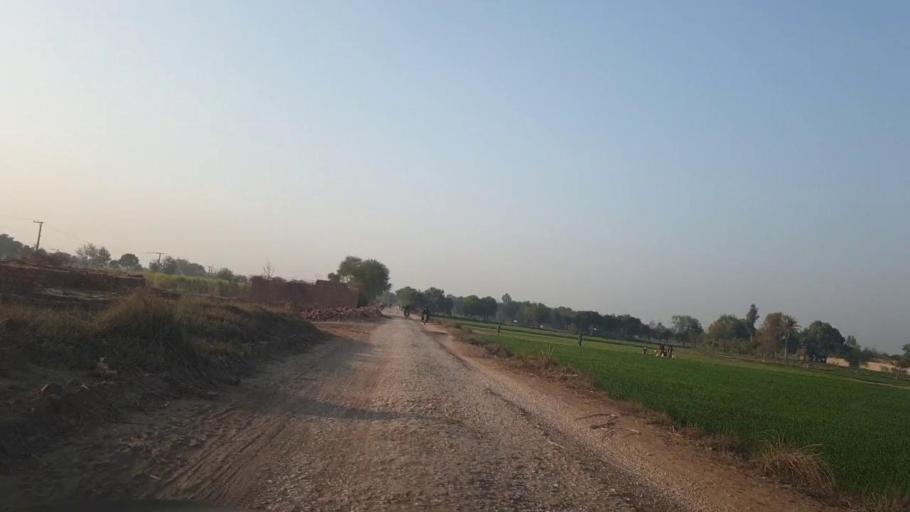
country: PK
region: Sindh
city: Ubauro
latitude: 28.3144
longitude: 69.7808
